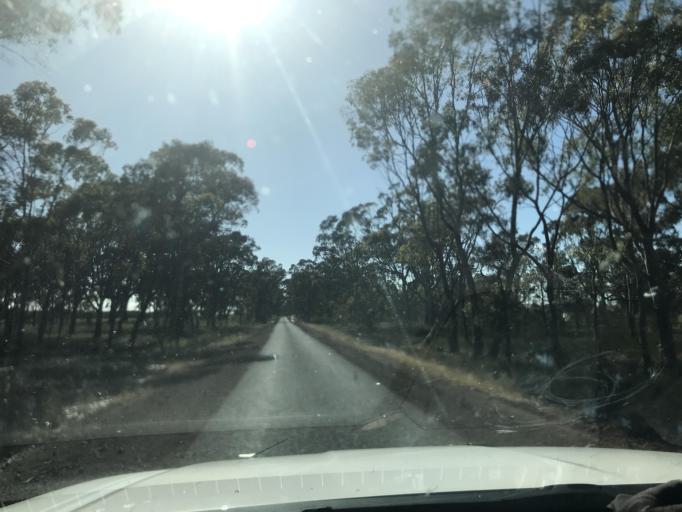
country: AU
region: Victoria
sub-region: Horsham
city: Horsham
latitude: -37.0248
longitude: 141.7011
